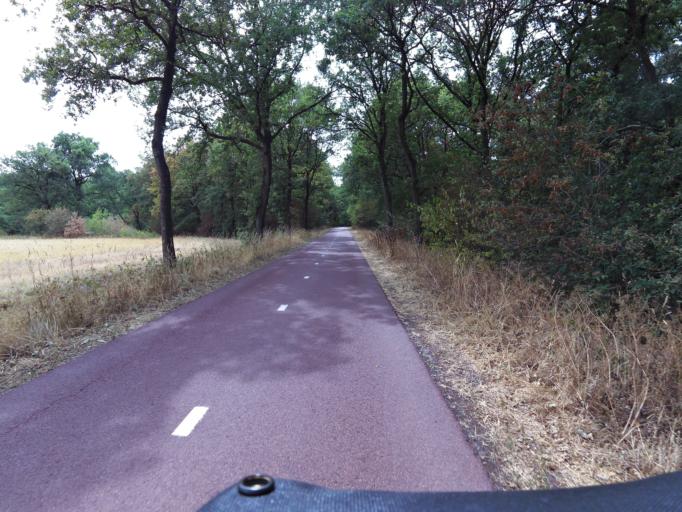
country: NL
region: Limburg
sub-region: Gemeente Venlo
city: Arcen
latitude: 51.5113
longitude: 6.1792
